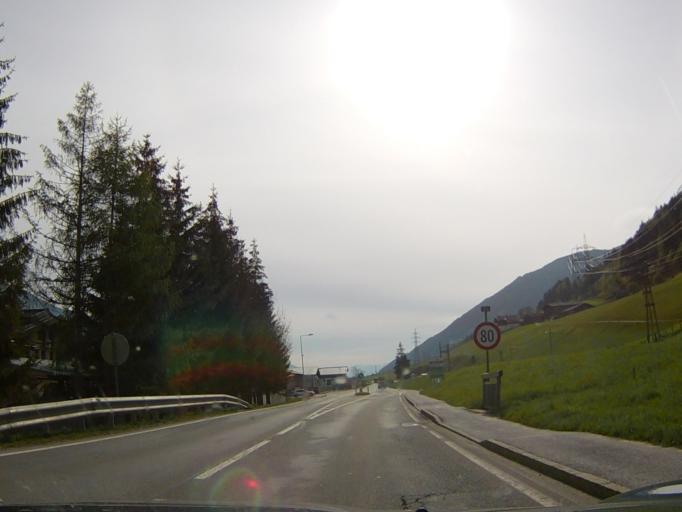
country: AT
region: Salzburg
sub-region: Politischer Bezirk Zell am See
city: Hollersbach im Pinzgau
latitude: 47.2761
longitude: 12.4415
